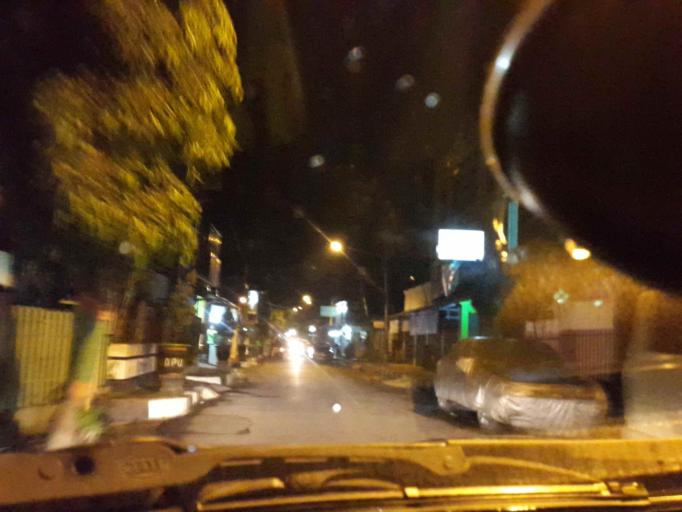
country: ID
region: Central Java
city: Wonosobo
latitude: -7.3676
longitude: 109.9036
